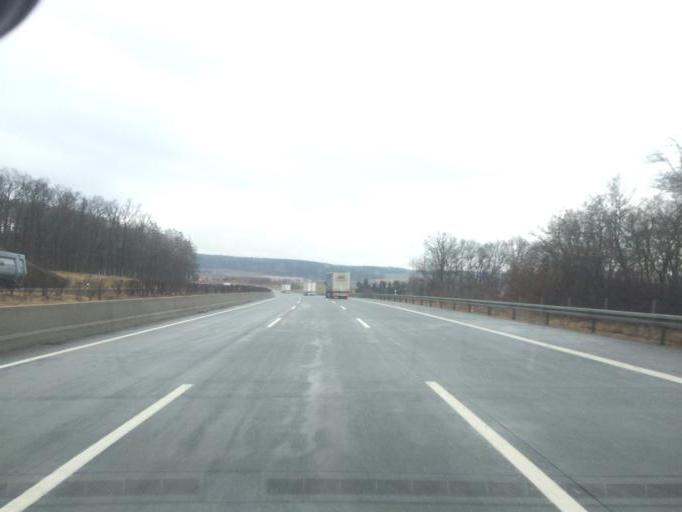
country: DE
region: Thuringia
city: Miesitz
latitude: 50.7348
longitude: 11.8498
